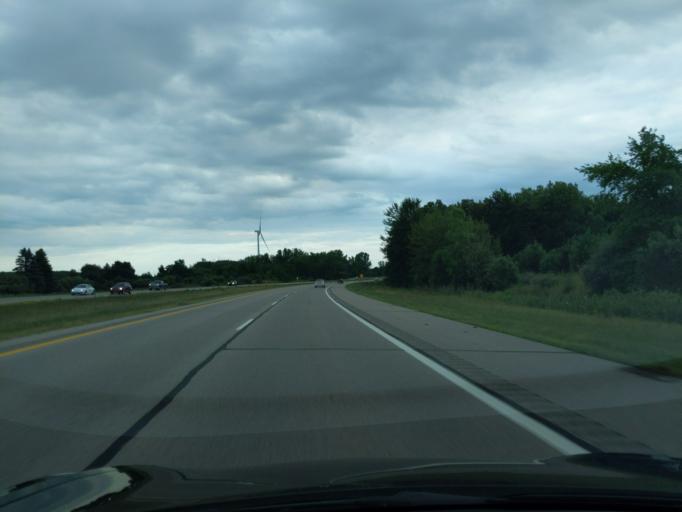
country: US
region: Michigan
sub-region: Isabella County
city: Shepherd
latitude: 43.5382
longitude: -84.6785
